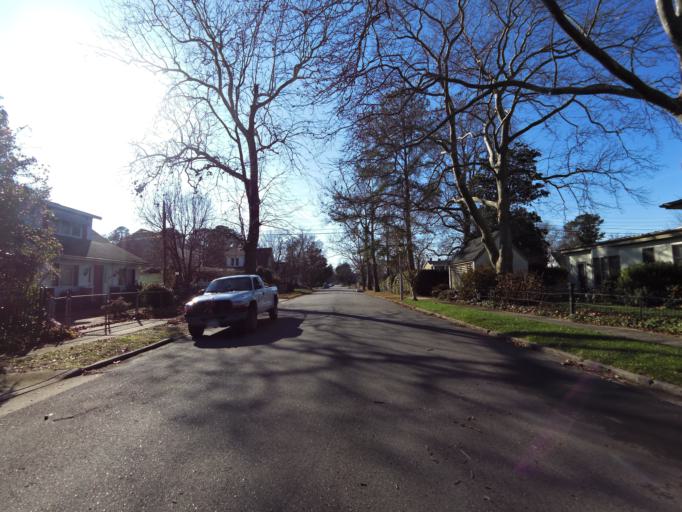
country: US
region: Virginia
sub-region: City of Hampton
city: Hampton
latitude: 37.0040
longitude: -76.3726
